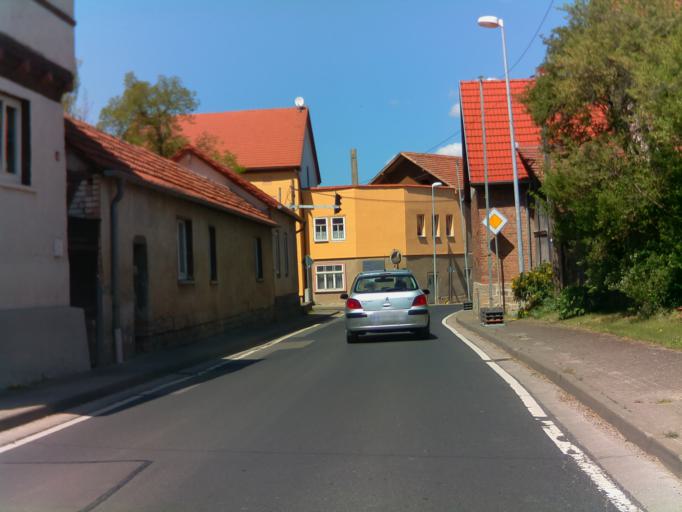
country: DE
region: Thuringia
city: Dornheim
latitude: 50.7960
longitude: 10.9820
